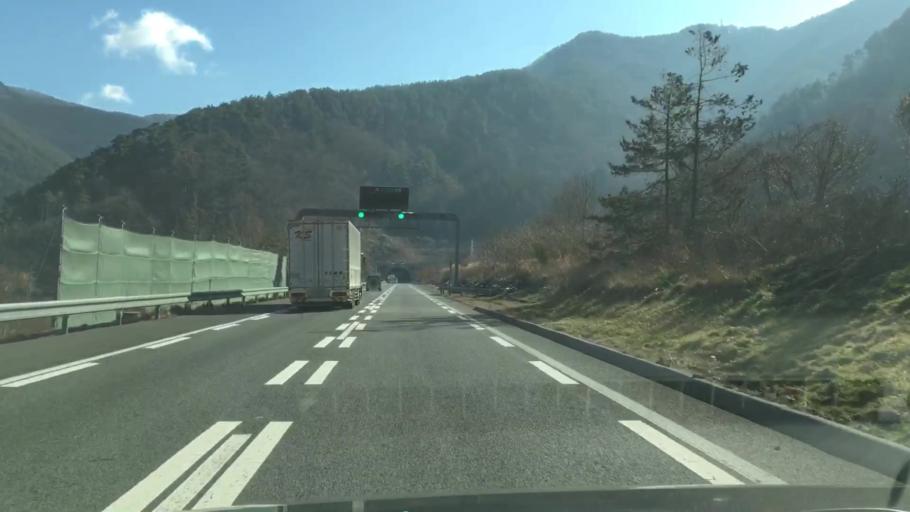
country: JP
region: Nagano
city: Nagano-shi
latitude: 36.5113
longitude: 138.1556
